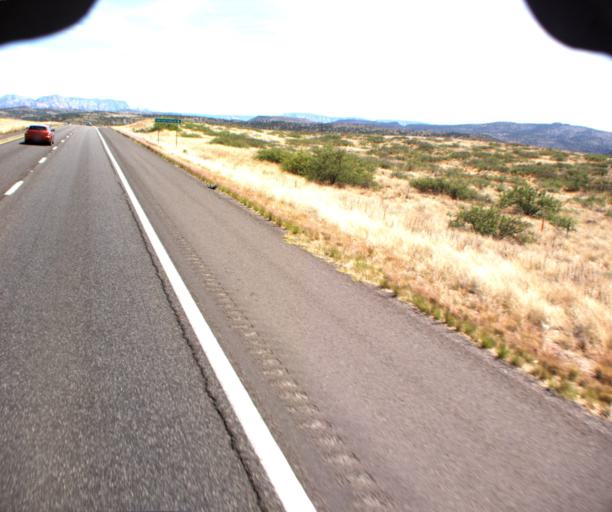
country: US
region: Arizona
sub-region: Yavapai County
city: Cornville
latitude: 34.7678
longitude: -111.9392
